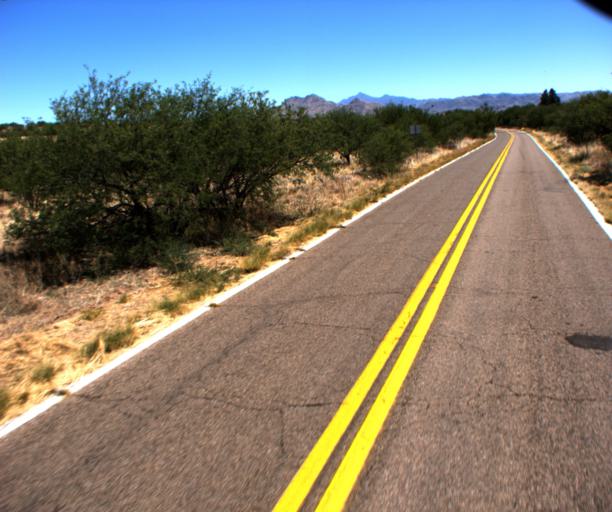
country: US
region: Arizona
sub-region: Santa Cruz County
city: Rio Rico
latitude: 31.4227
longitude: -111.0118
